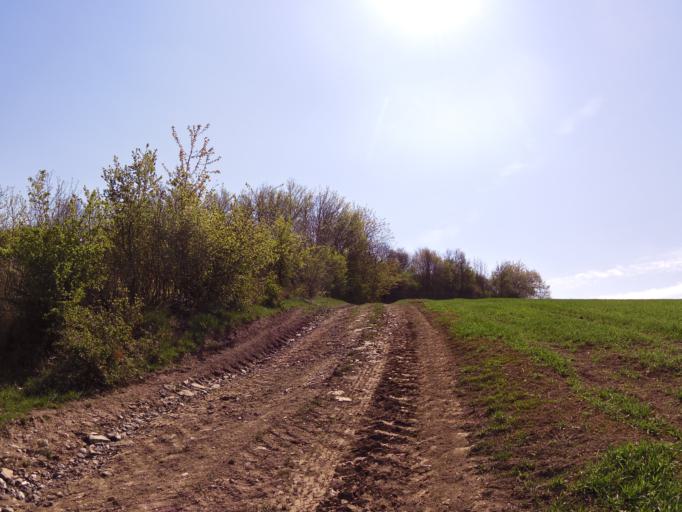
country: DE
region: Bavaria
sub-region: Regierungsbezirk Unterfranken
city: Biebelried
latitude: 49.7861
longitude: 10.0680
